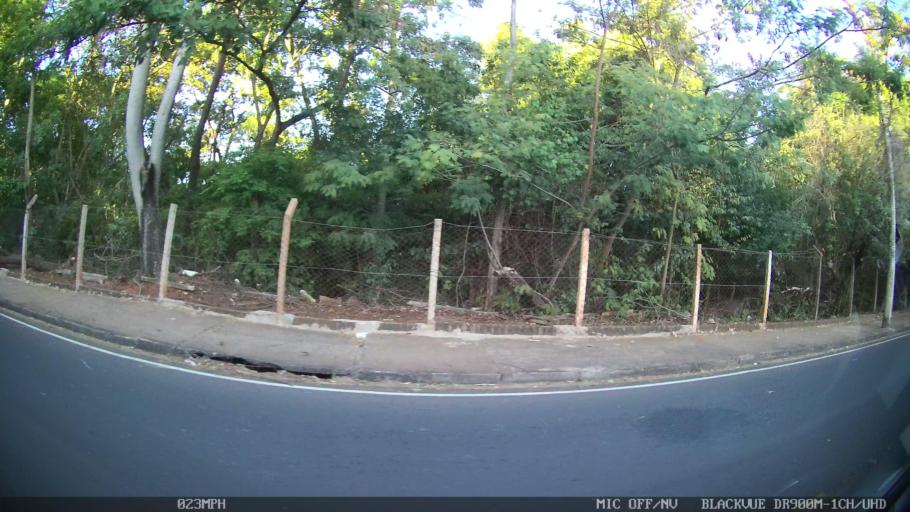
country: BR
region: Sao Paulo
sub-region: Sao Jose Do Rio Preto
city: Sao Jose do Rio Preto
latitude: -20.7772
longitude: -49.3561
